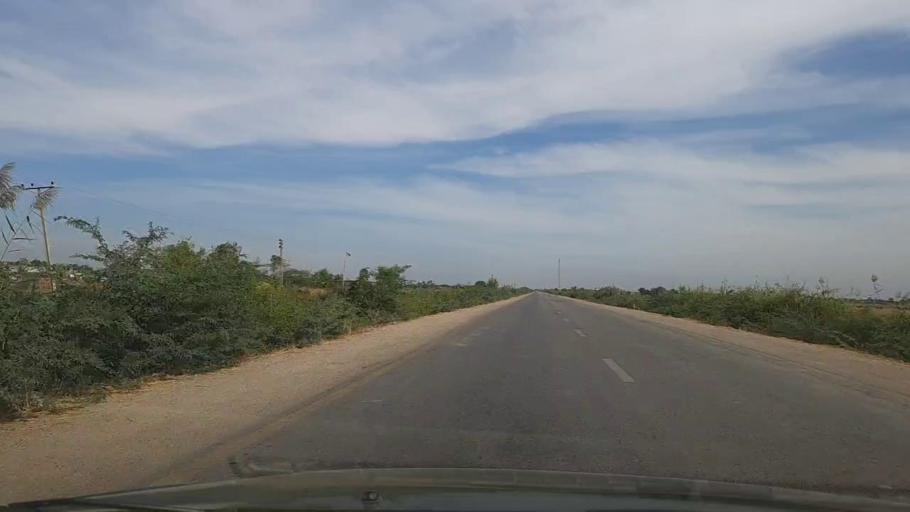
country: PK
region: Sindh
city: Thatta
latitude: 24.8047
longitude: 67.9695
